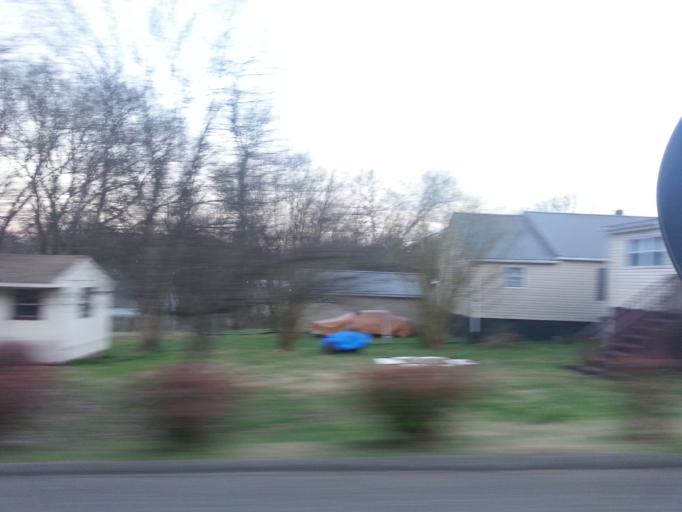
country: US
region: Tennessee
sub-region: Knox County
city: Knoxville
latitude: 35.9494
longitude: -83.8895
